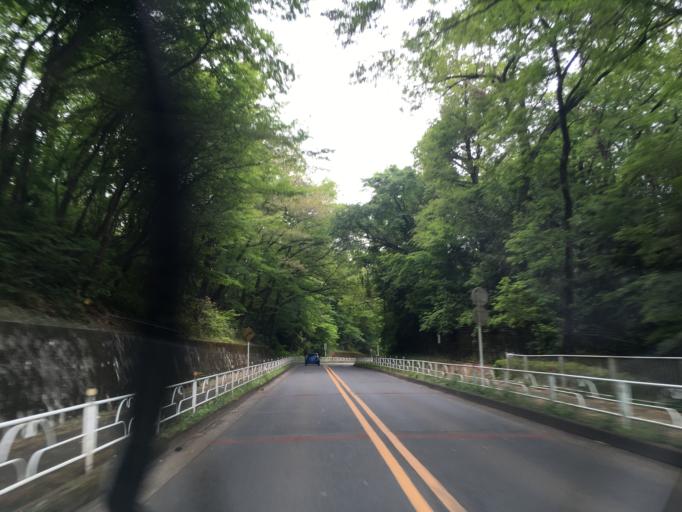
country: JP
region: Tokyo
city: Higashimurayama-shi
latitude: 35.7641
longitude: 139.3940
